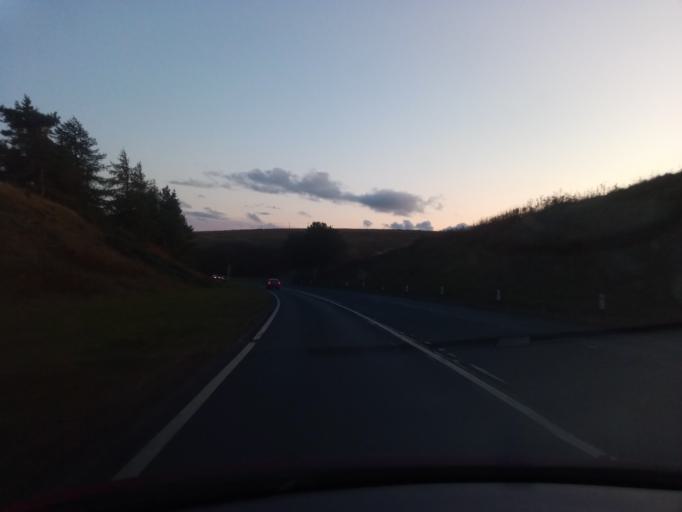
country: GB
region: Scotland
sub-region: East Lothian
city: Pencaitland
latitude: 55.8012
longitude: -2.8382
